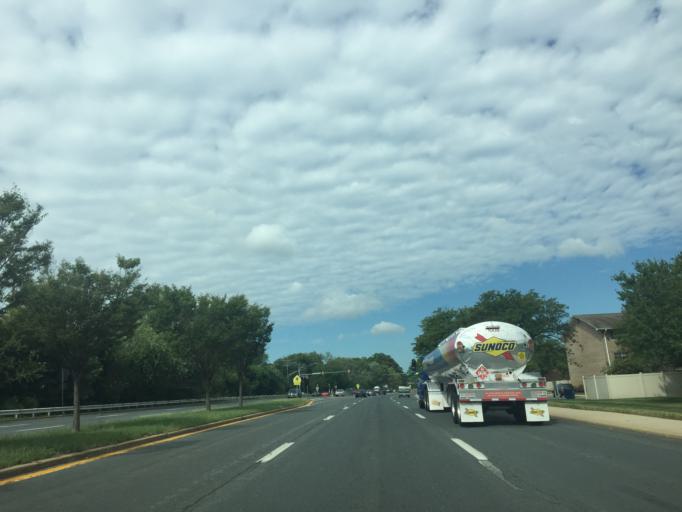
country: US
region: Maryland
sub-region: Prince George's County
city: Laurel
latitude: 39.1017
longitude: -76.8637
